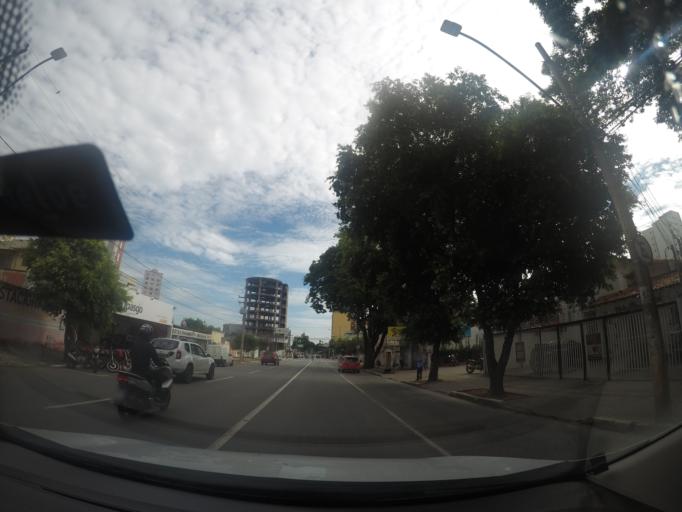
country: BR
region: Goias
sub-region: Goiania
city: Goiania
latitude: -16.6777
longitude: -49.2556
